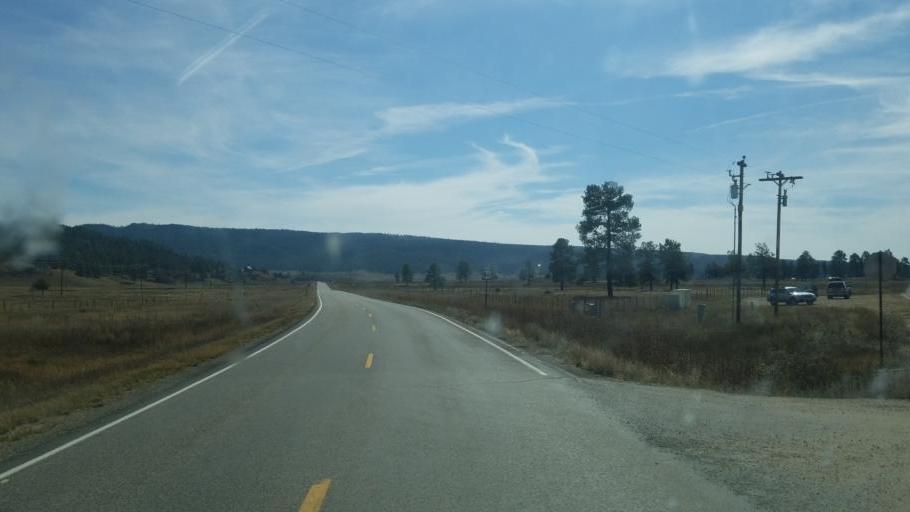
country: US
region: New Mexico
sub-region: Rio Arriba County
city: Dulce
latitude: 37.0936
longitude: -106.9098
